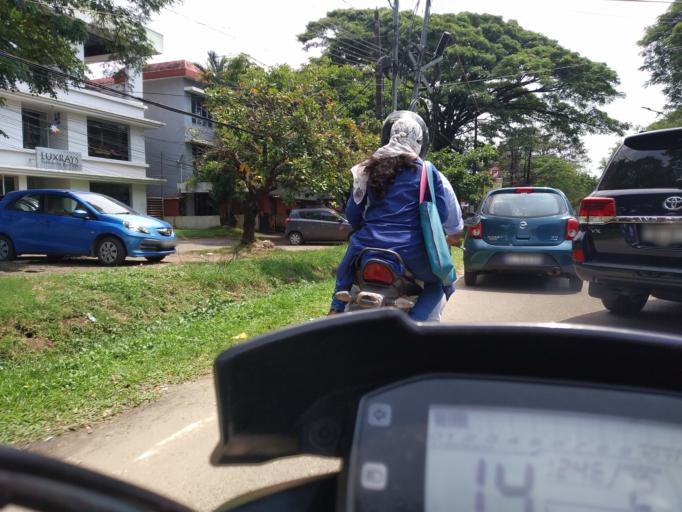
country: IN
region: Kerala
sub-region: Ernakulam
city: Cochin
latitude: 9.9610
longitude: 76.2958
